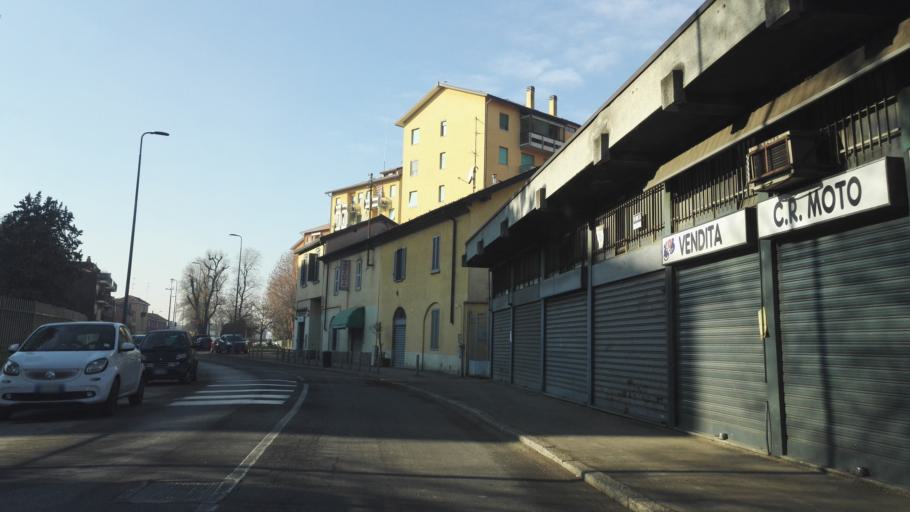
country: IT
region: Lombardy
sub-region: Citta metropolitana di Milano
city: Chiaravalle
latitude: 45.4447
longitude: 9.2441
